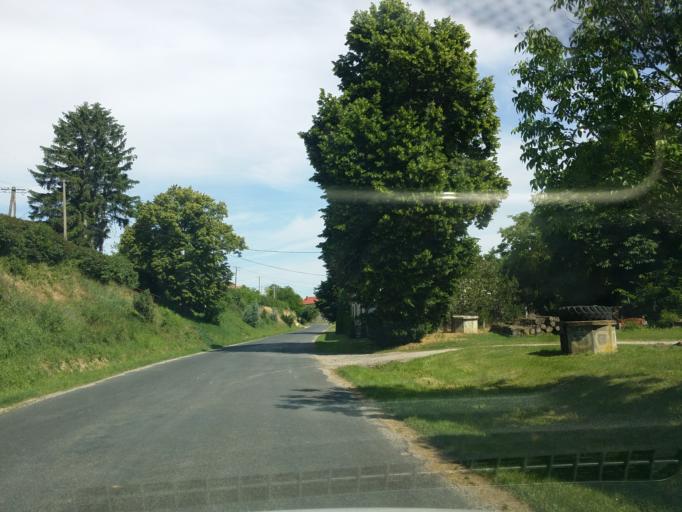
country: HU
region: Zala
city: Zalaszentgrot
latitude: 46.8867
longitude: 17.0727
